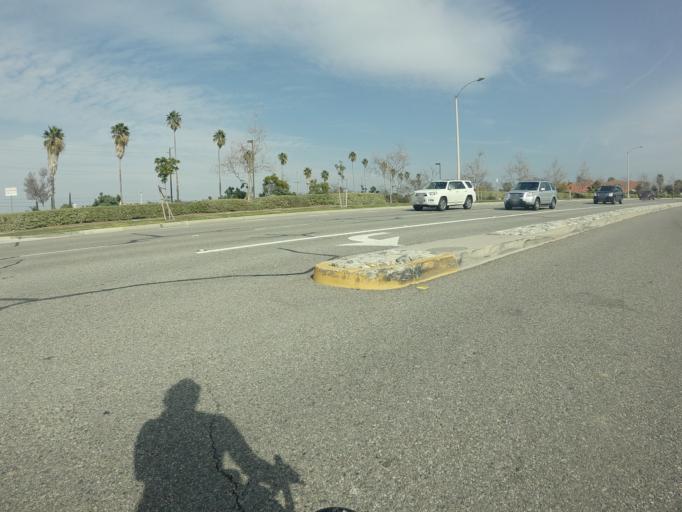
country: US
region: California
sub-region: Riverside County
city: Corona
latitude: 33.8447
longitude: -117.5737
